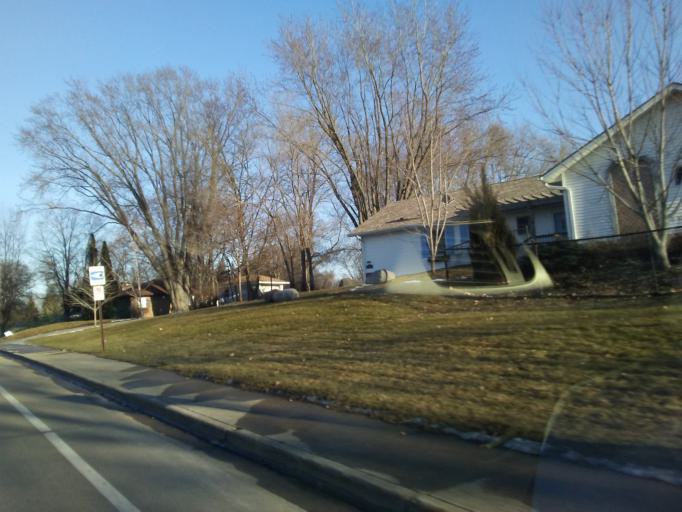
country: US
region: Minnesota
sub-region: Hennepin County
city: Bloomington
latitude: 44.8480
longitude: -93.3034
